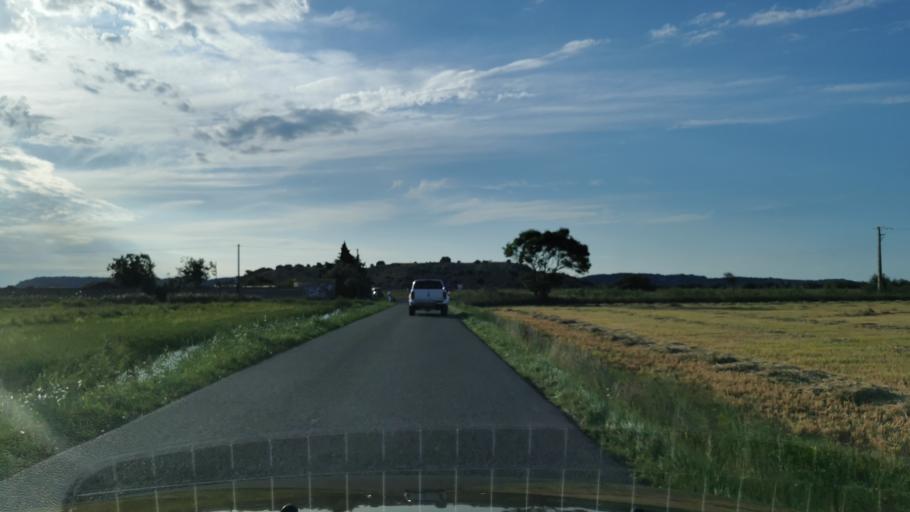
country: FR
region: Languedoc-Roussillon
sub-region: Departement de l'Aude
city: Gruissan
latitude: 43.1158
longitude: 3.0395
